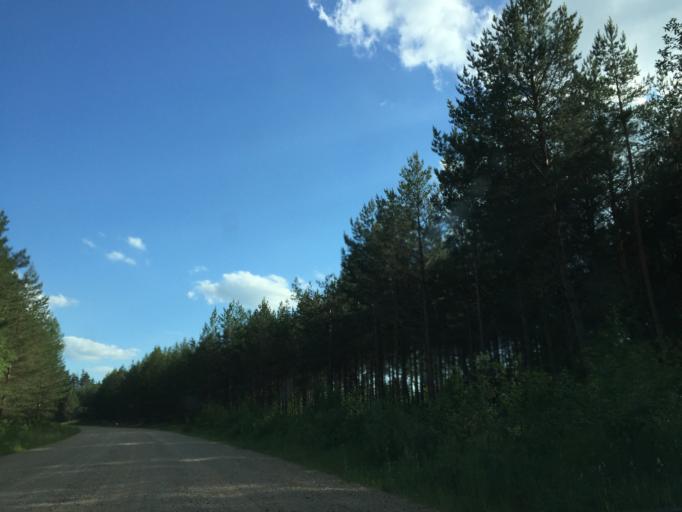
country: LV
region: Kandava
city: Kandava
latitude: 56.8540
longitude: 22.7498
